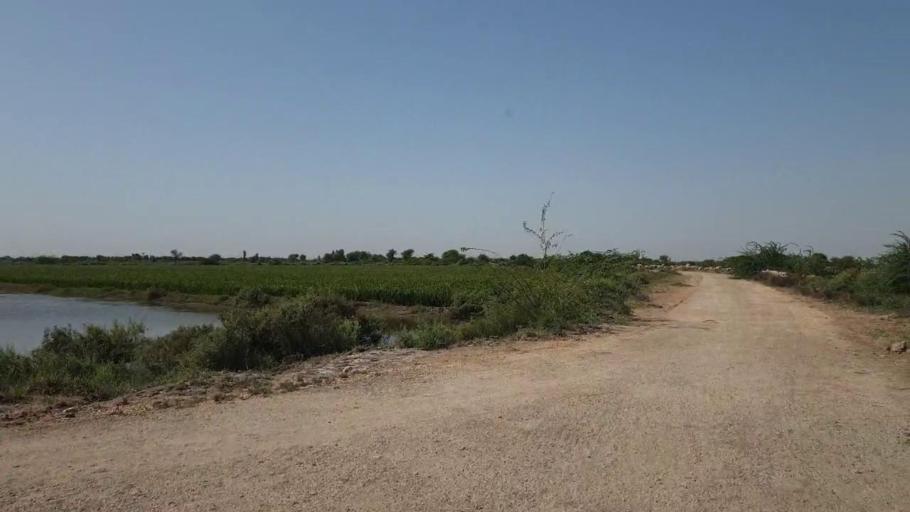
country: PK
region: Sindh
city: Tando Bago
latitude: 24.7057
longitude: 69.0560
